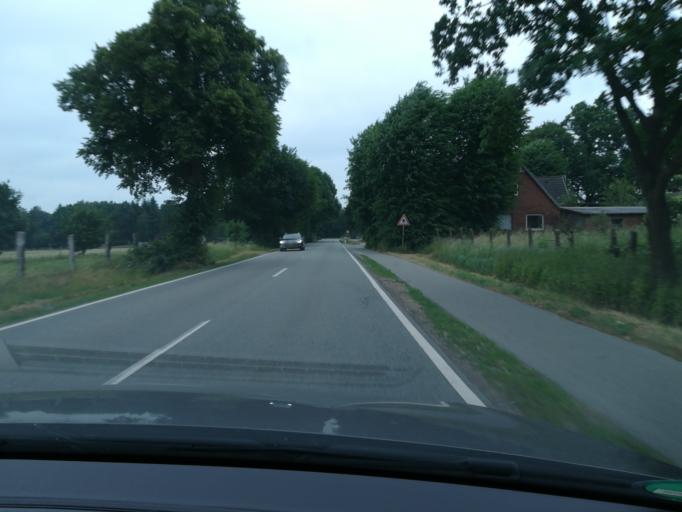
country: DE
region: Schleswig-Holstein
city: Grossensee
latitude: 53.6130
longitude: 10.3664
